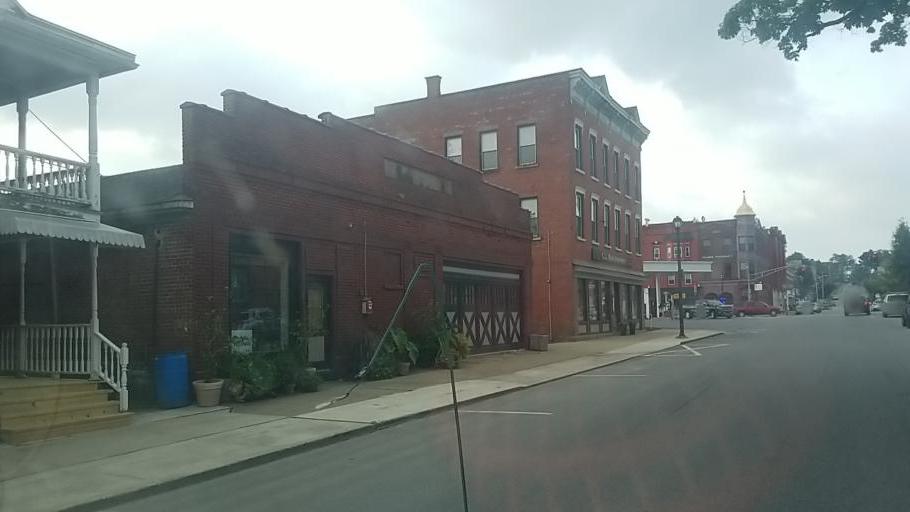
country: US
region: New York
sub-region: Fulton County
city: Johnstown
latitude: 43.0073
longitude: -74.3713
